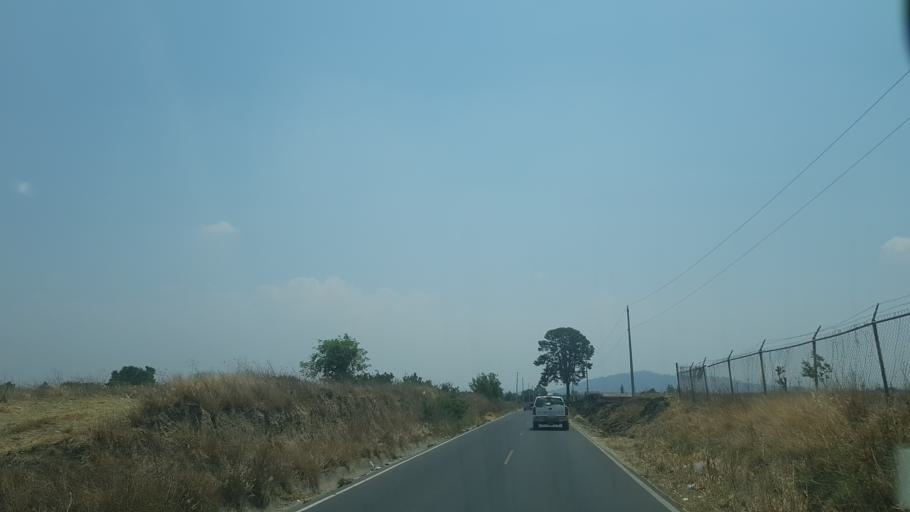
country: MX
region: Puebla
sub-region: San Jeronimo Tecuanipan
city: San Miguel Papaxtla
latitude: 19.0956
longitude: -98.4087
